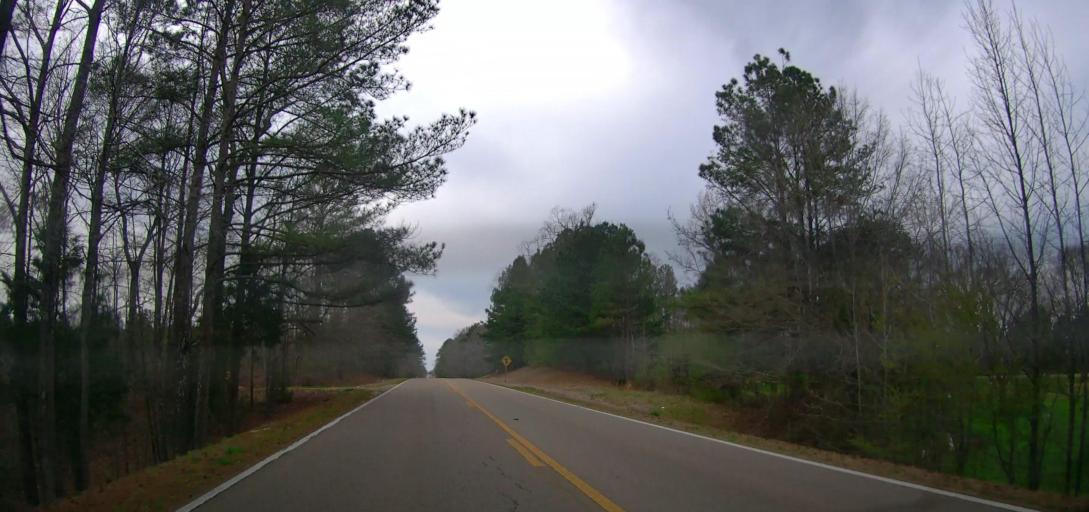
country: US
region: Mississippi
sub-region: Itawamba County
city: Mantachie
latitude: 34.2570
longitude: -88.5014
